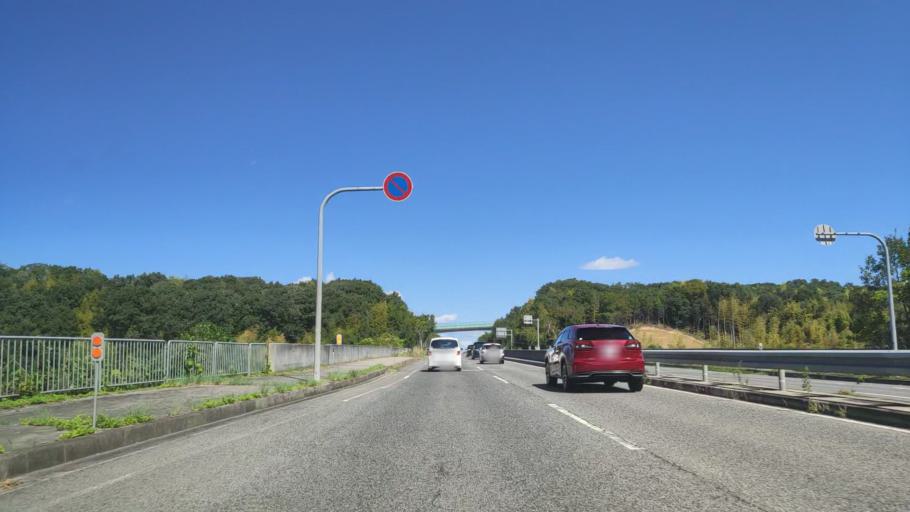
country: JP
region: Hyogo
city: Ono
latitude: 34.8239
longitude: 134.9503
